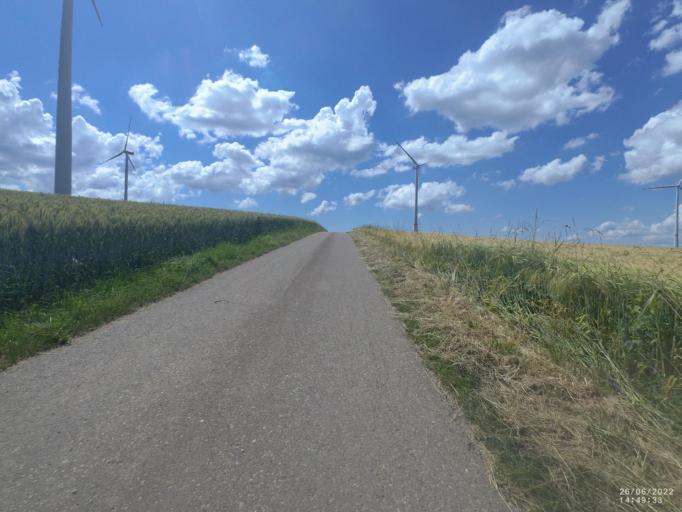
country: DE
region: Baden-Wuerttemberg
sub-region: Regierungsbezirk Stuttgart
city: Bohmenkirch
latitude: 48.6585
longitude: 9.9385
